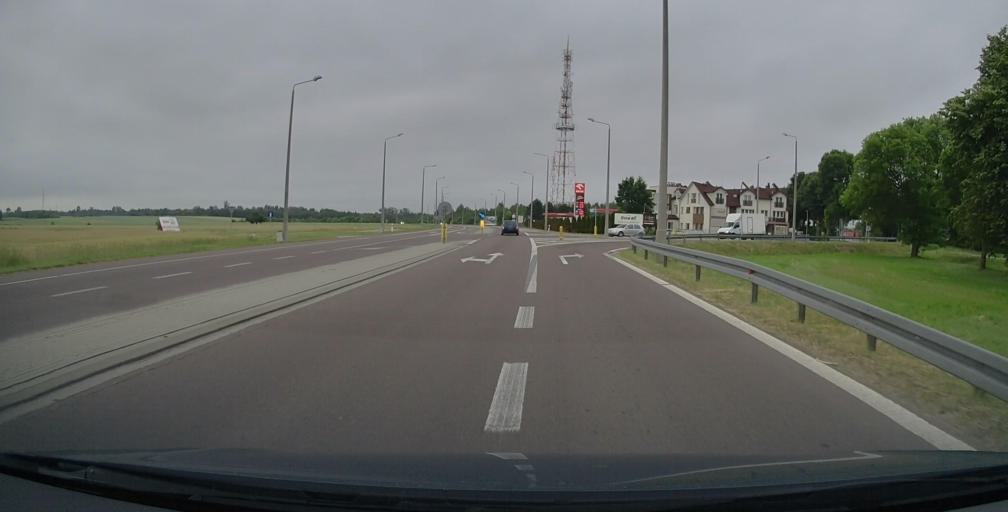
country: PL
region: Lublin Voivodeship
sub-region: Biala Podlaska
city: Biala Podlaska
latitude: 52.0338
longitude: 23.0663
